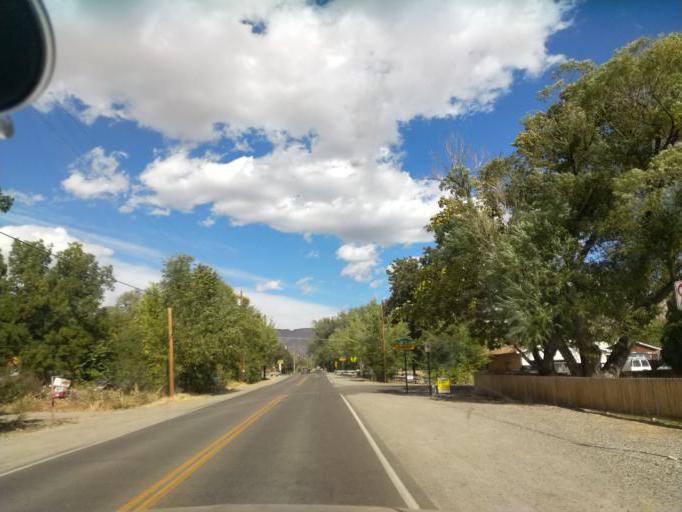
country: US
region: Colorado
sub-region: Mesa County
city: Clifton
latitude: 39.0945
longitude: -108.4408
